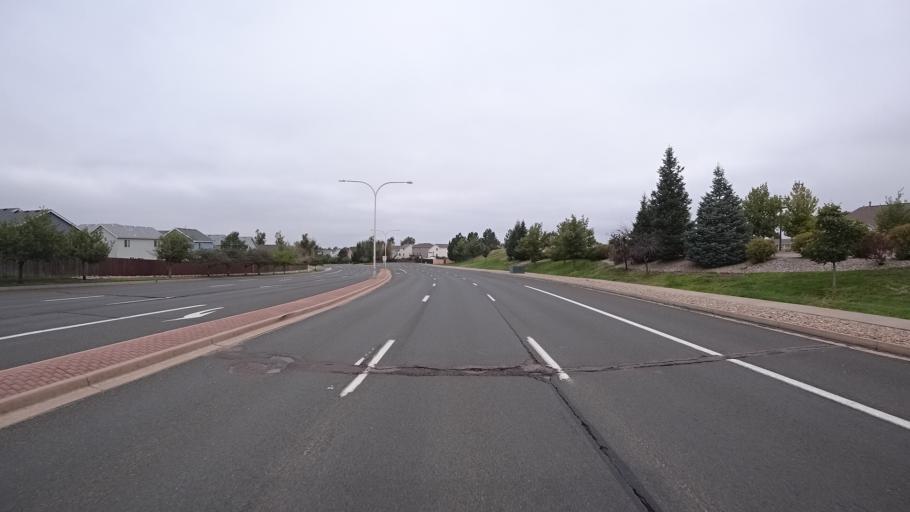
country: US
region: Colorado
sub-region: El Paso County
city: Cimarron Hills
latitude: 38.9095
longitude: -104.6957
